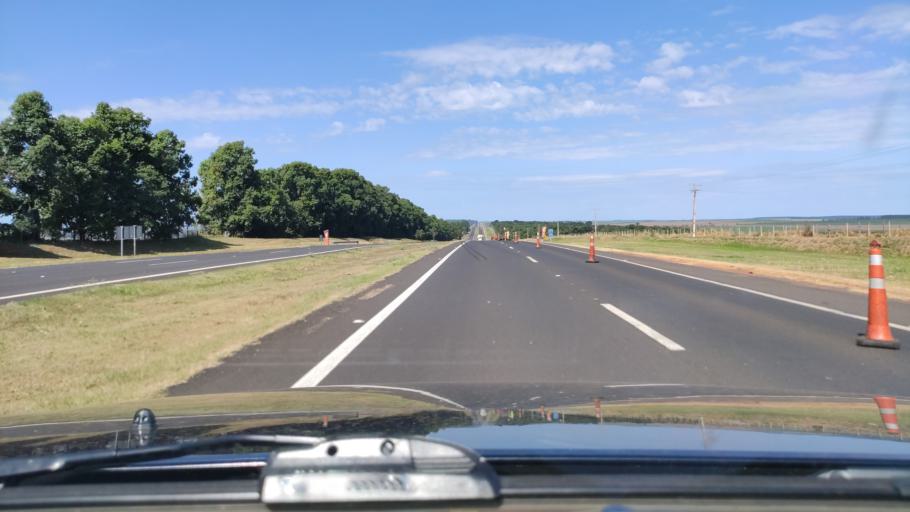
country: BR
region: Sao Paulo
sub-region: Rancharia
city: Rancharia
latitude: -22.3973
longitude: -51.0739
